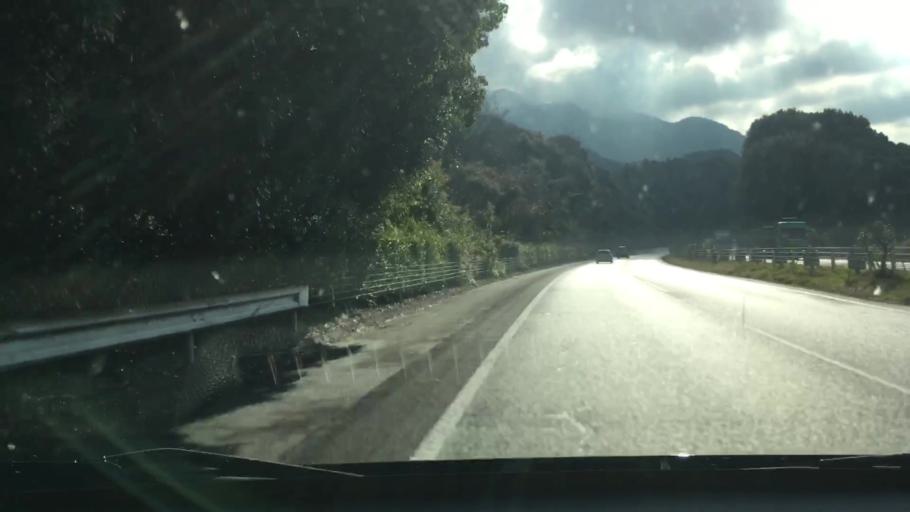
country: JP
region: Kumamoto
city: Matsubase
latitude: 32.5530
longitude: 130.6942
